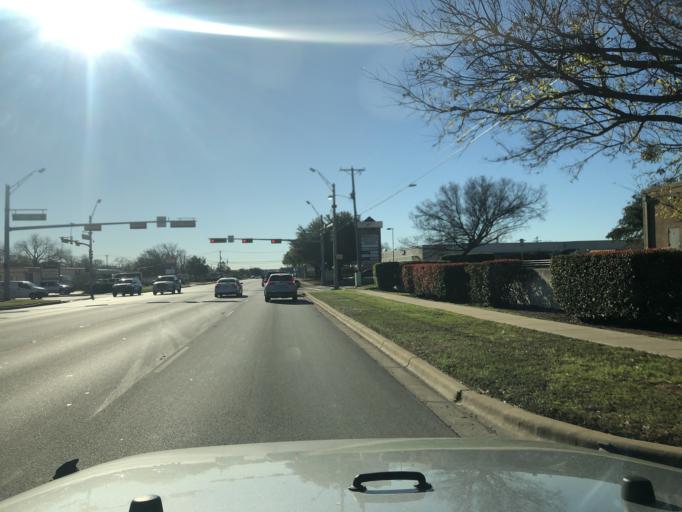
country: US
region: Texas
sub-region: Williamson County
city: Round Rock
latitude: 30.5294
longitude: -97.6887
